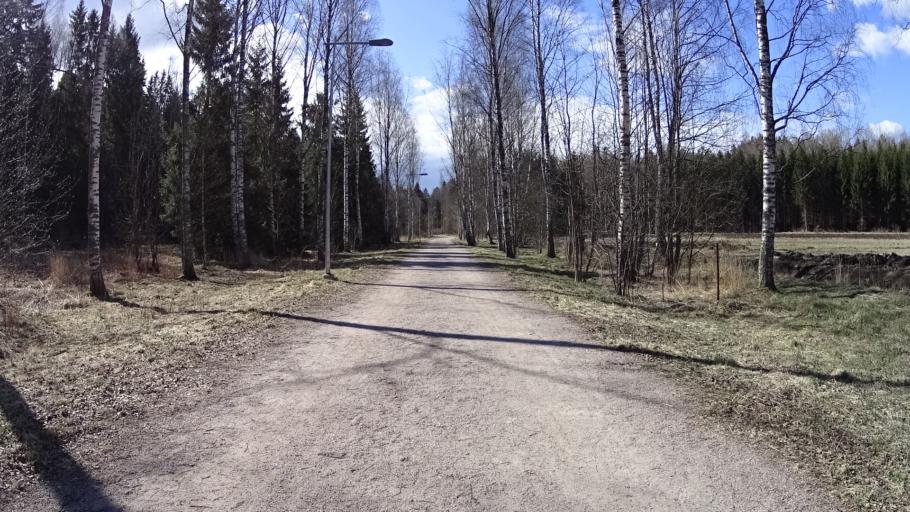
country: FI
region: Uusimaa
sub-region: Helsinki
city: Kilo
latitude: 60.2366
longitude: 24.7954
